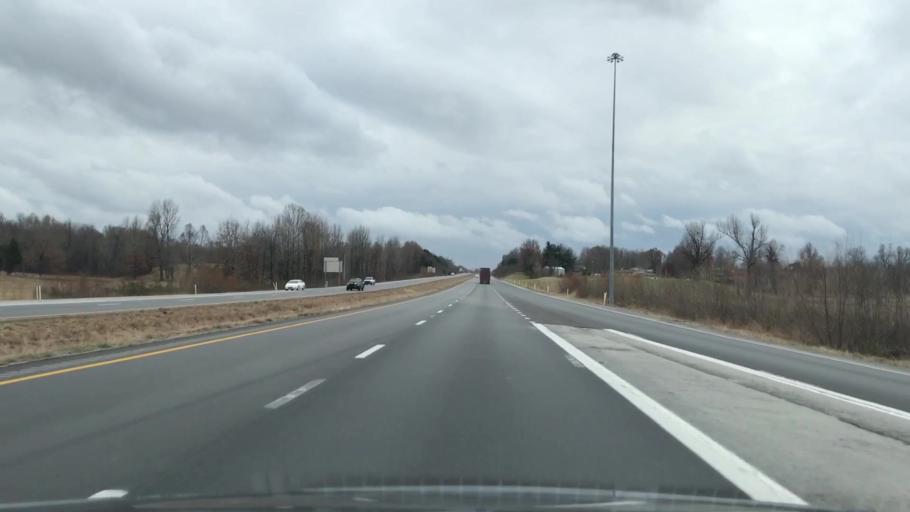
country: US
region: Kentucky
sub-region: Hopkins County
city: Madisonville
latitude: 37.4135
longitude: -87.4734
